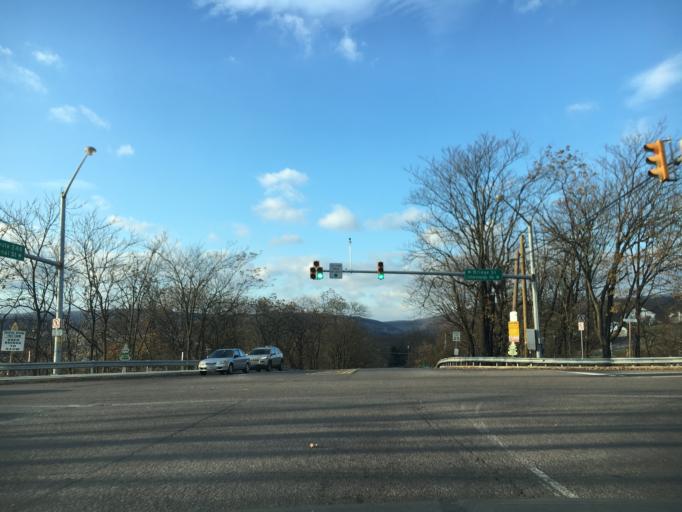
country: US
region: Pennsylvania
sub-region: Carbon County
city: Weissport East
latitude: 40.8290
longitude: -75.6988
